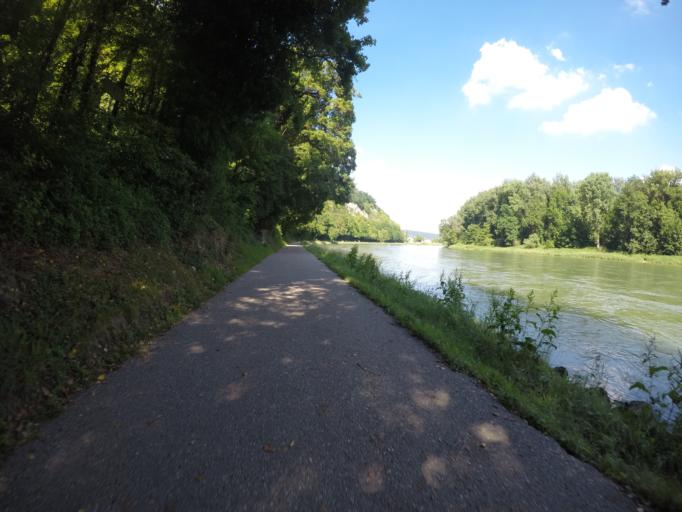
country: DE
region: Bavaria
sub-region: Lower Bavaria
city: Ihrlerstein
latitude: 48.9152
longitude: 11.8543
